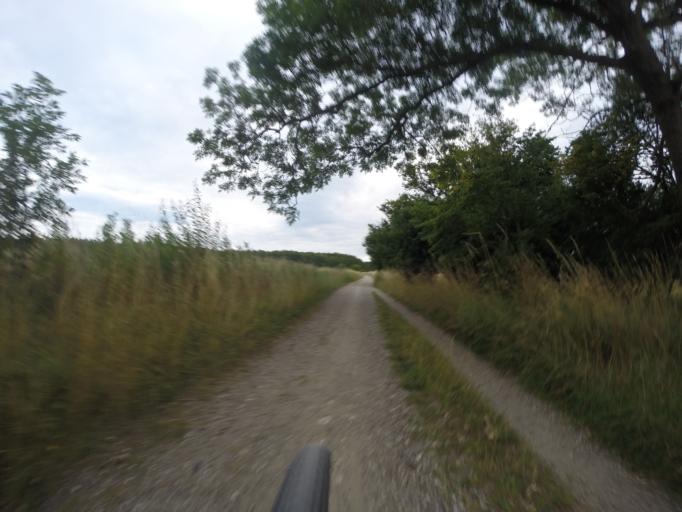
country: DK
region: Capital Region
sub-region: Hoje-Taastrup Kommune
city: Taastrup
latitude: 55.6918
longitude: 12.3180
